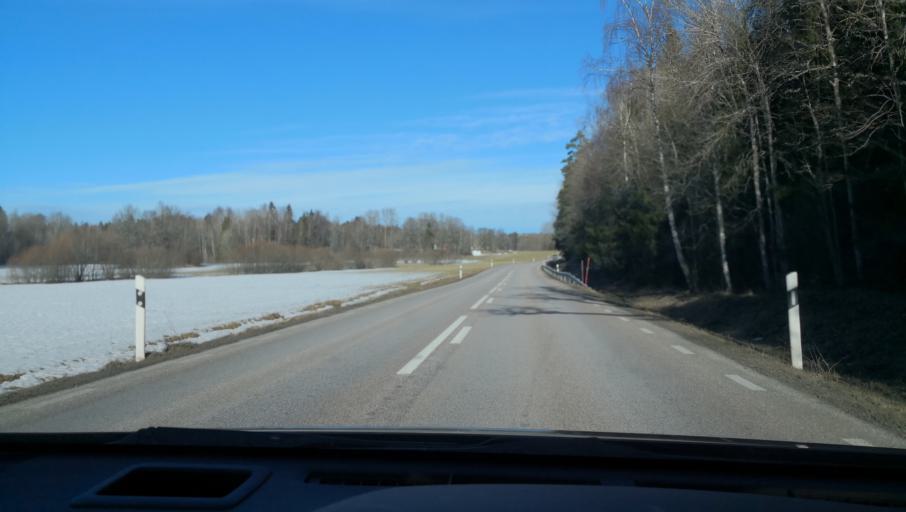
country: SE
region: Uppsala
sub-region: Osthammars Kommun
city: Osterbybruk
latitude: 60.1380
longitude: 17.8163
